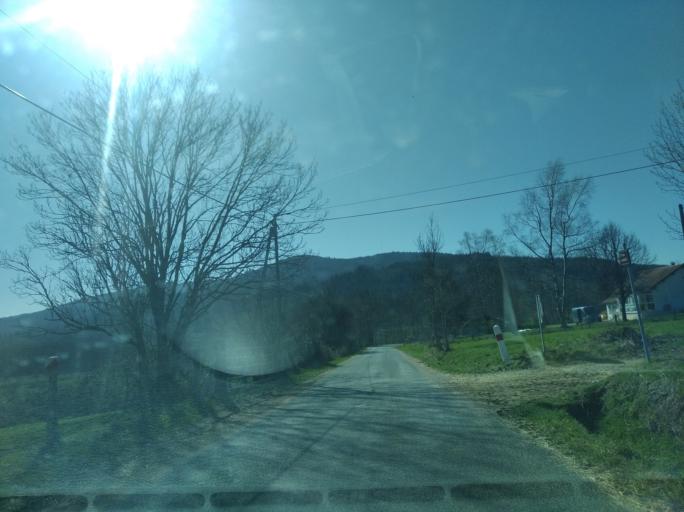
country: FR
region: Rhone-Alpes
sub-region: Departement de la Loire
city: La Pacaudiere
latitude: 46.1151
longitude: 3.7965
